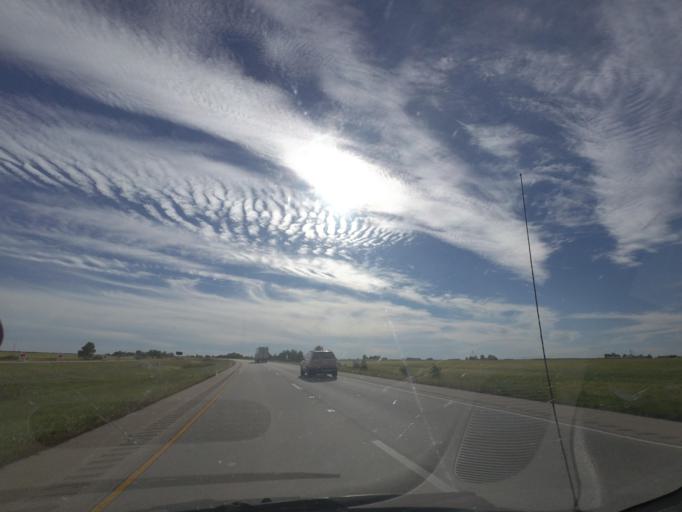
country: US
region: Illinois
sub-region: Piatt County
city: Cerro Gordo
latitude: 39.9735
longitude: -88.8073
